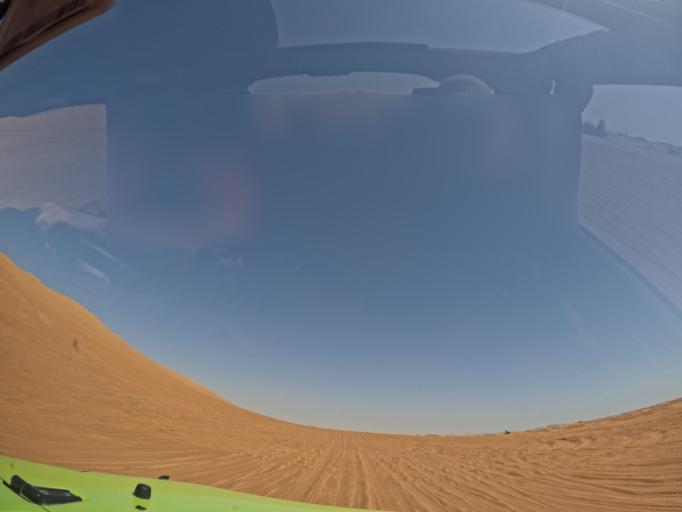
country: AE
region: Ash Shariqah
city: Adh Dhayd
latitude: 24.9591
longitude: 55.7200
